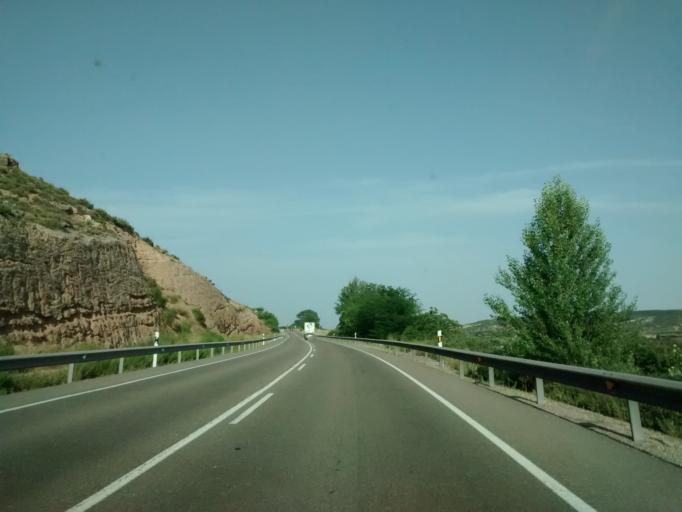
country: ES
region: Aragon
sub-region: Provincia de Zaragoza
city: Bulbuente
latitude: 41.8182
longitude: -1.6183
